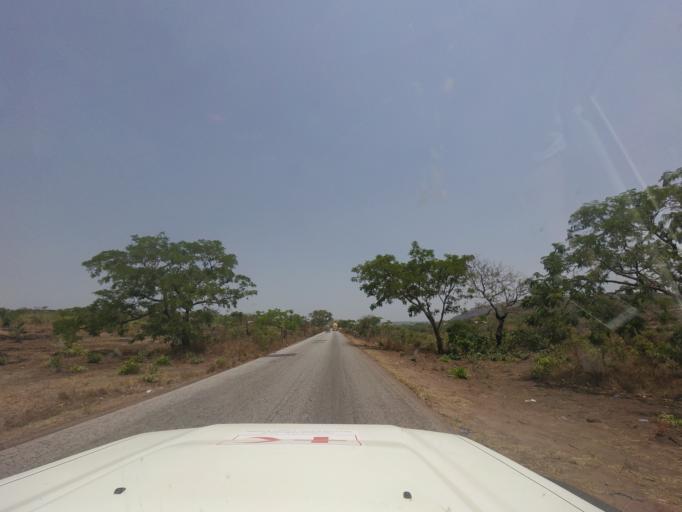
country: GN
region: Kindia
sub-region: Coyah
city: Coyah
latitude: 9.8270
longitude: -13.1170
